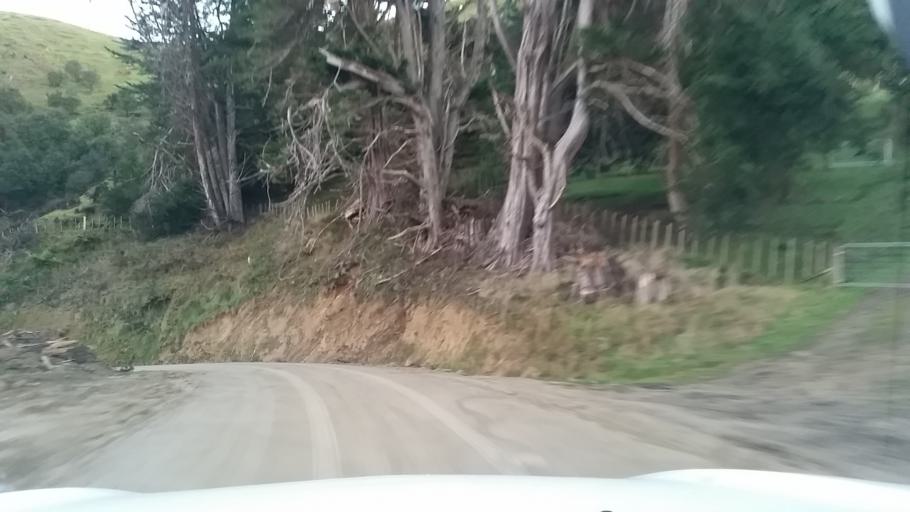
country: NZ
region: Manawatu-Wanganui
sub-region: Wanganui District
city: Wanganui
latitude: -39.7516
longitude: 174.8883
